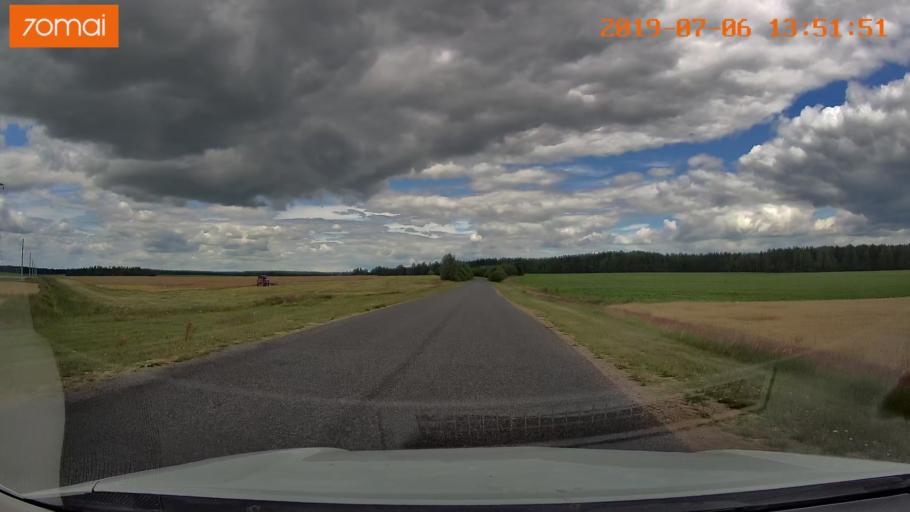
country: BY
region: Minsk
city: Ivyanyets
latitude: 53.7132
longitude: 26.8291
